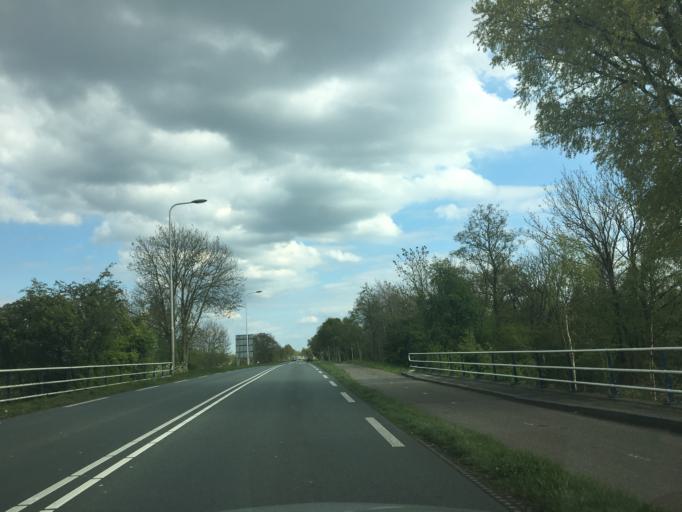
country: NL
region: Utrecht
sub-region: Stichtse Vecht
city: Vreeland
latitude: 52.2344
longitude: 5.0628
